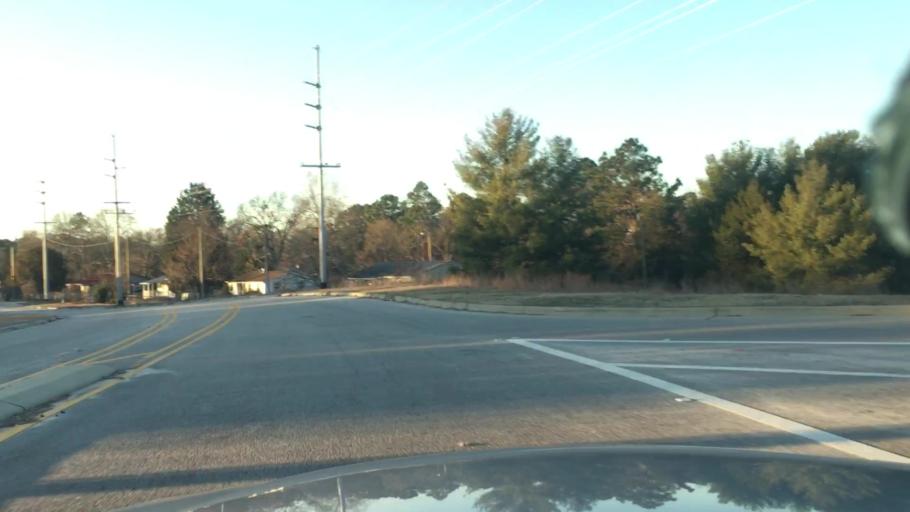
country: US
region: North Carolina
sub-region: Cumberland County
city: Hope Mills
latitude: 34.9983
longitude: -78.9341
